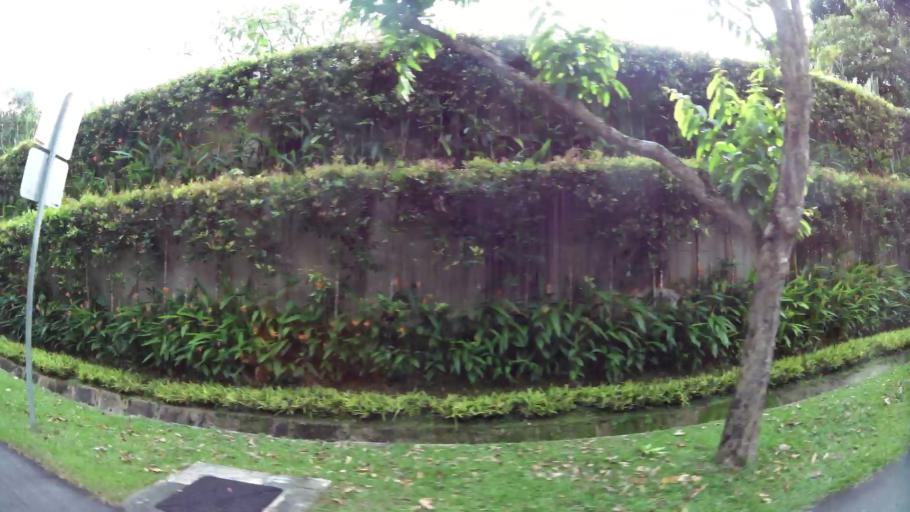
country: SG
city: Singapore
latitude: 1.3169
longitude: 103.7896
